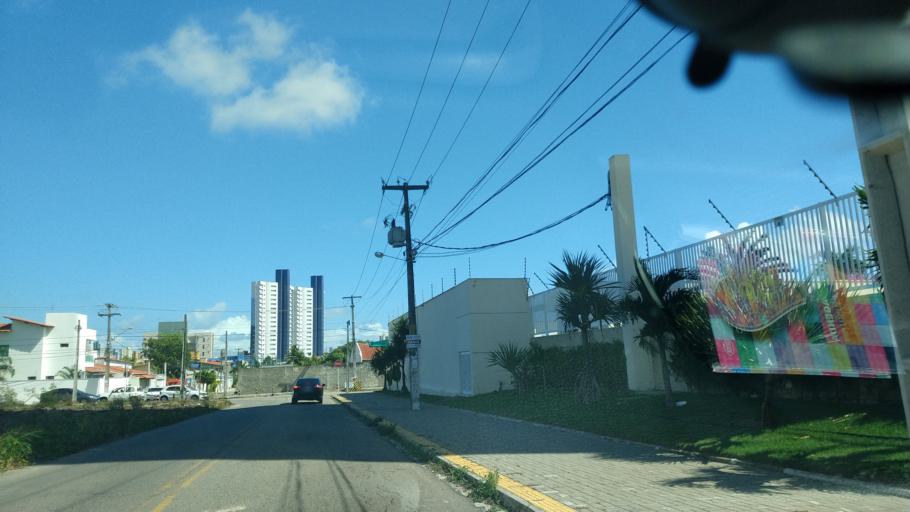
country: BR
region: Rio Grande do Norte
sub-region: Natal
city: Natal
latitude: -5.8696
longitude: -35.1940
